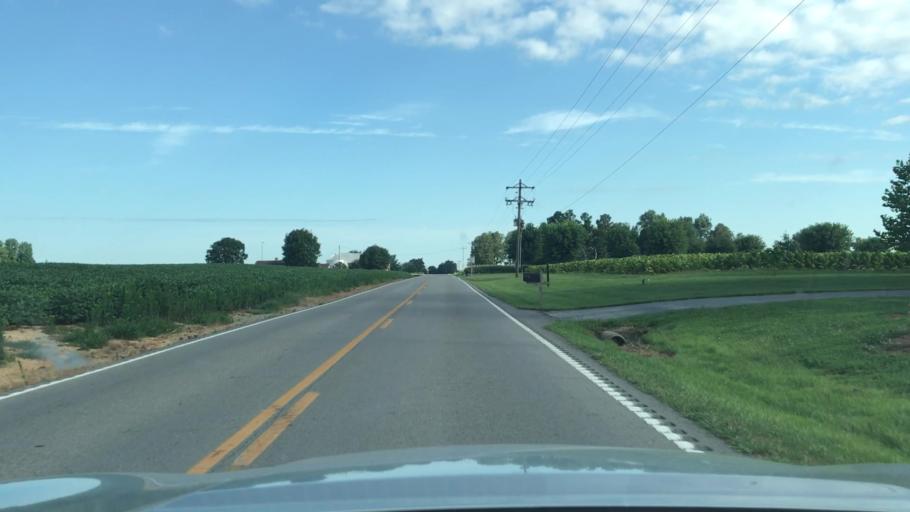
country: US
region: Kentucky
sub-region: Todd County
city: Elkton
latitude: 36.8684
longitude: -87.1635
